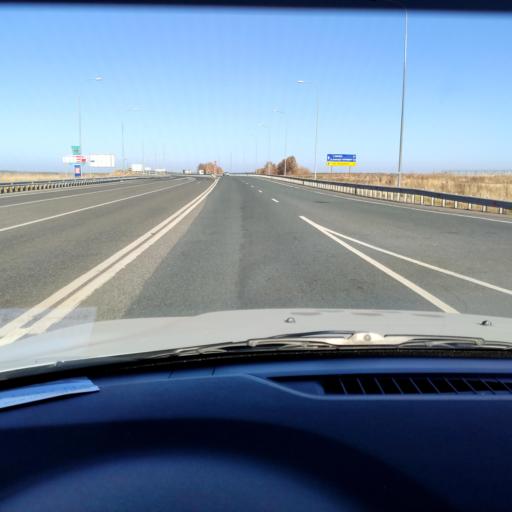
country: RU
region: Samara
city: Bereza
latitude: 53.4933
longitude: 50.1179
